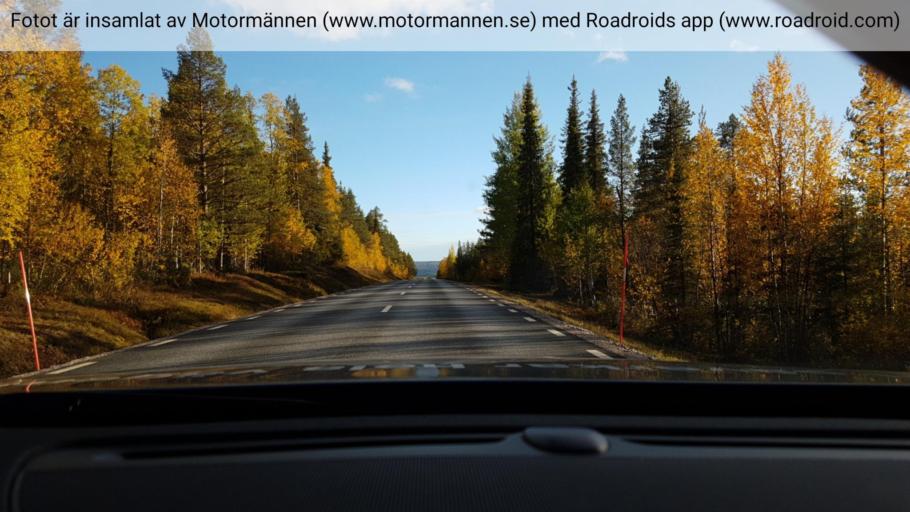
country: SE
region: Norrbotten
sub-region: Jokkmokks Kommun
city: Jokkmokk
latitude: 66.8979
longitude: 19.8270
